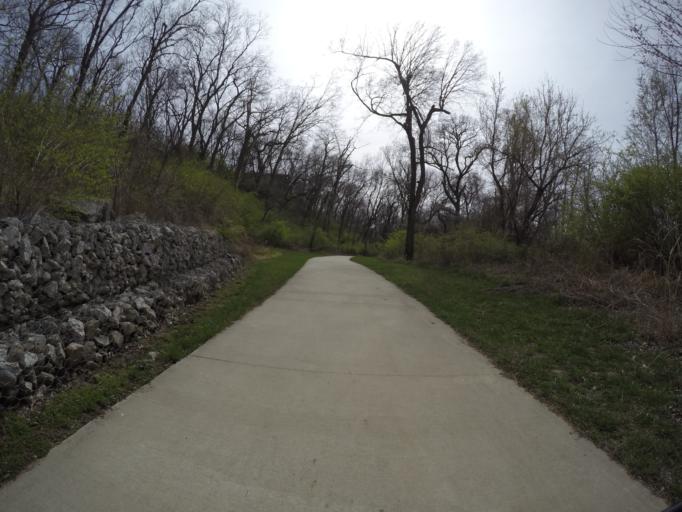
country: US
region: Kansas
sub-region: Johnson County
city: Leawood
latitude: 38.9537
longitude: -94.5724
